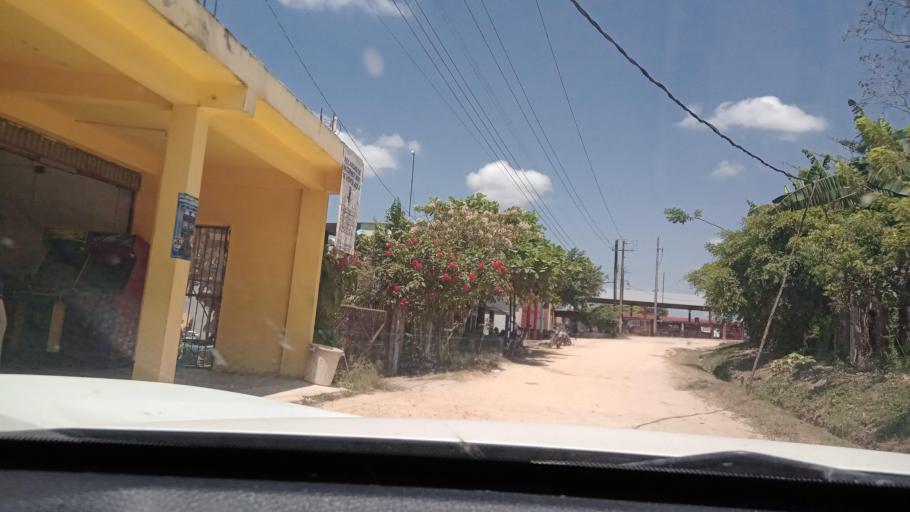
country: MX
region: Veracruz
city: Las Choapas
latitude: 17.7544
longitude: -94.1118
